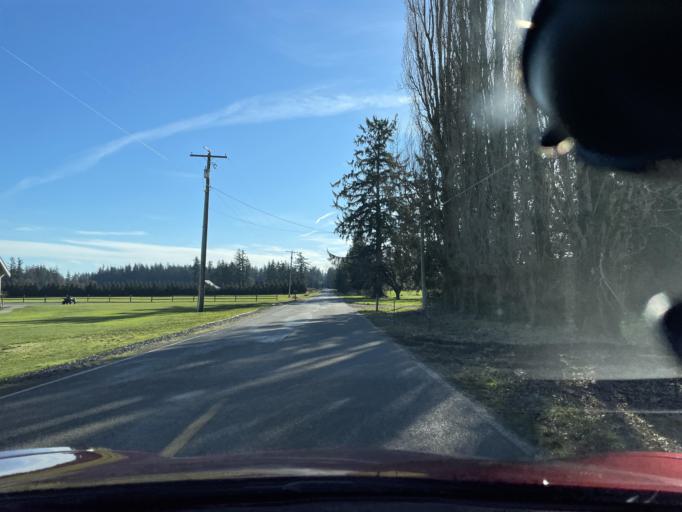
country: US
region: Washington
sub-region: Whatcom County
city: Lynden
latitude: 48.9800
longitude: -122.5129
